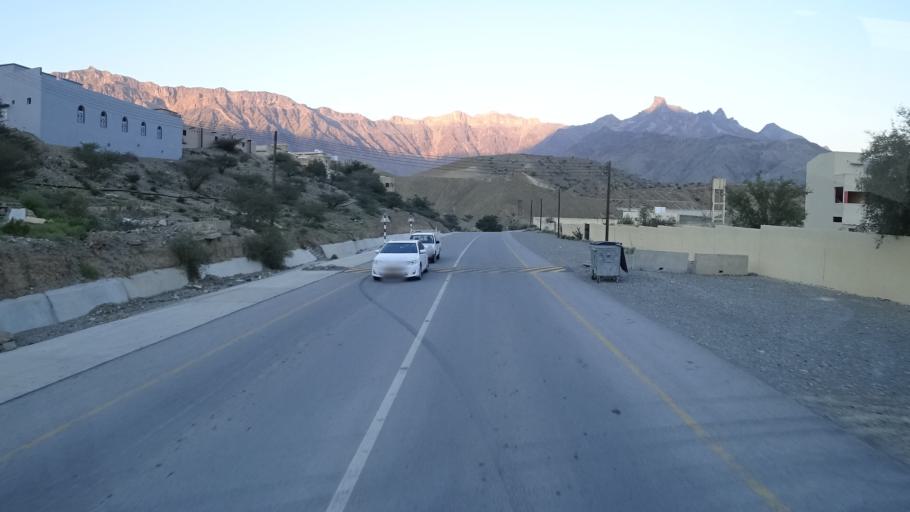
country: OM
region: Al Batinah
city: Rustaq
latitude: 23.2847
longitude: 57.3306
